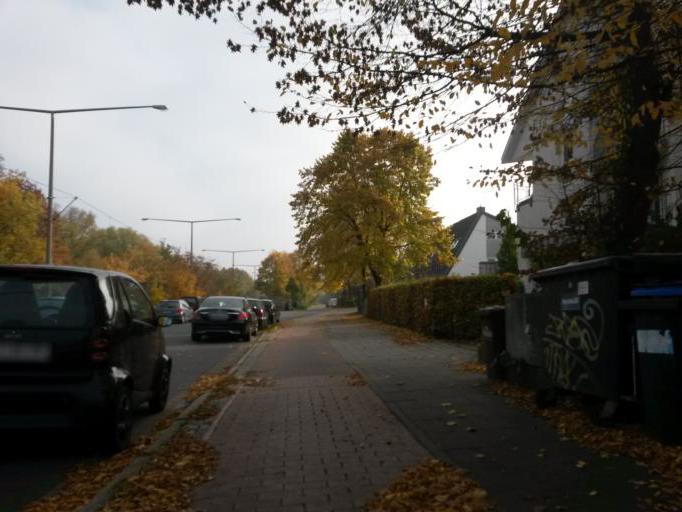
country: DE
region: Bremen
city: Bremen
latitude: 53.0814
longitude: 8.8558
